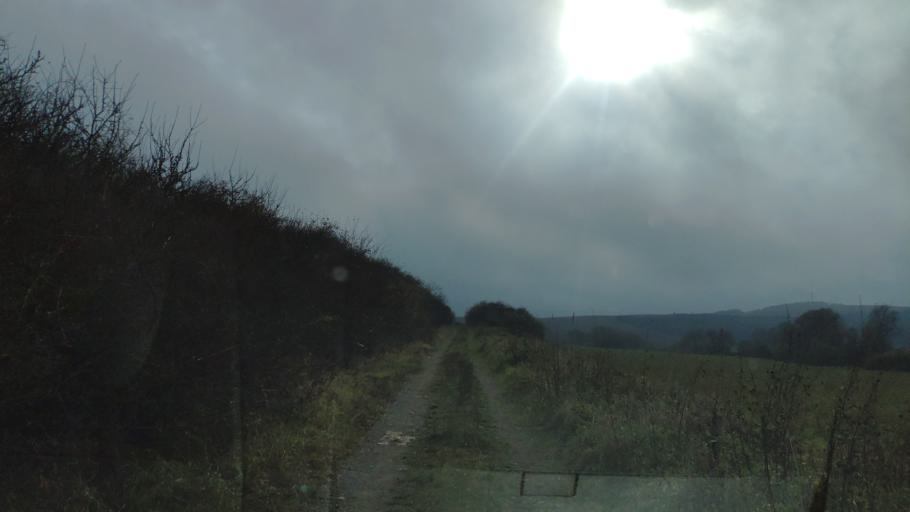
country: SK
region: Presovsky
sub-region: Okres Presov
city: Presov
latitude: 49.0206
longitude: 21.1997
